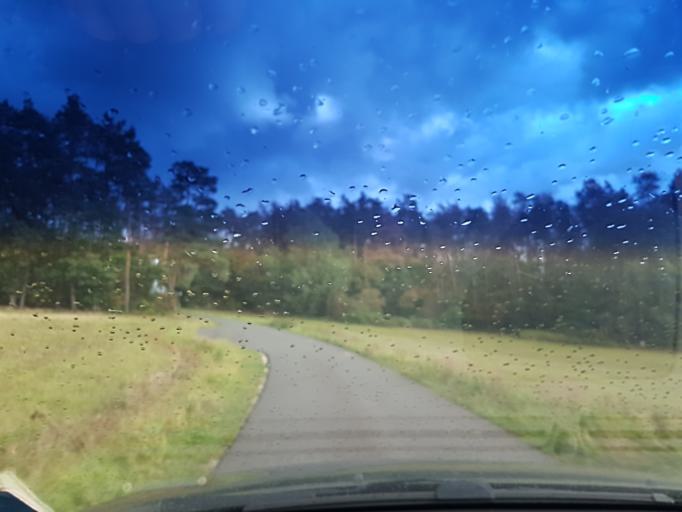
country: DE
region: Bavaria
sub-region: Regierungsbezirk Mittelfranken
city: Burghaslach
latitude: 49.7508
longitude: 10.5791
